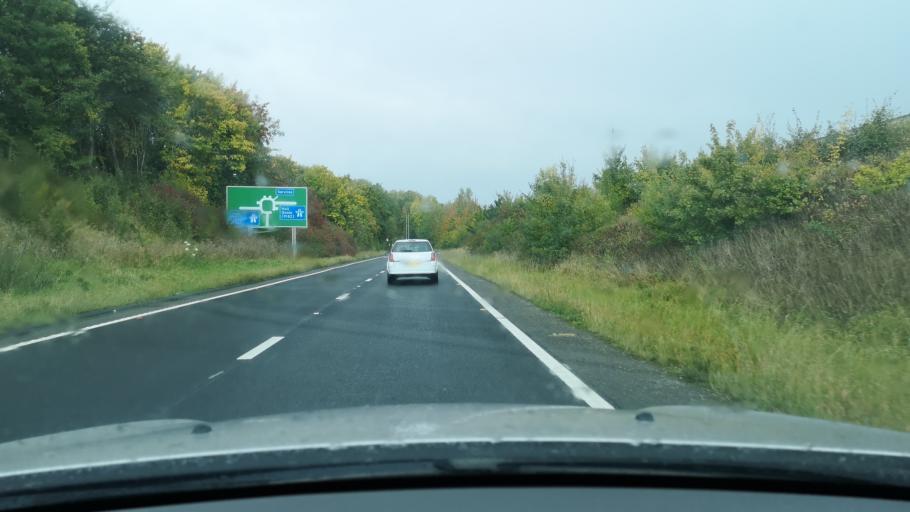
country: GB
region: England
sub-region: City and Borough of Wakefield
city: Darrington
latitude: 53.6922
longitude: -1.2670
